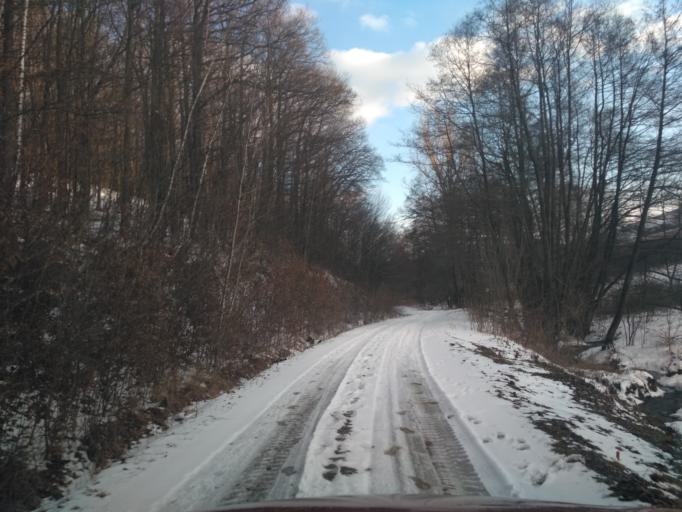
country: SK
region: Kosicky
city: Kosice
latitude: 48.7437
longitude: 21.1526
